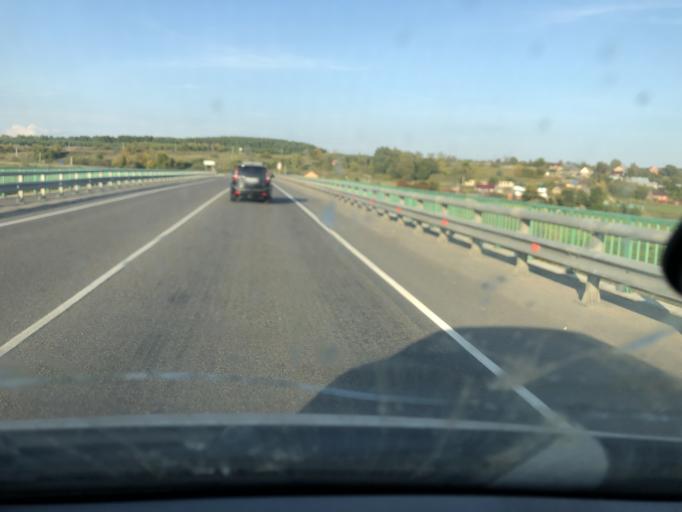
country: RU
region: Kaluga
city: Peremyshl'
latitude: 54.2926
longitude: 36.1757
